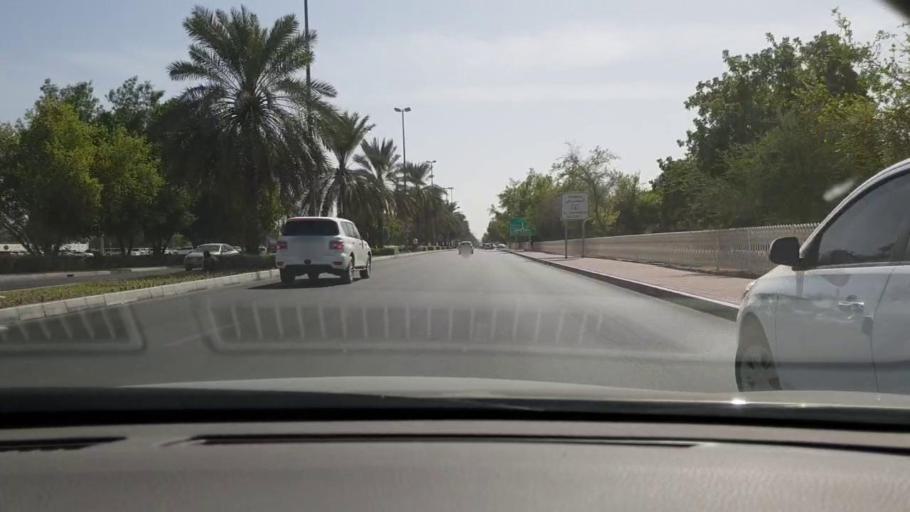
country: AE
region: Abu Dhabi
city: Al Ain
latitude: 24.2344
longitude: 55.7385
